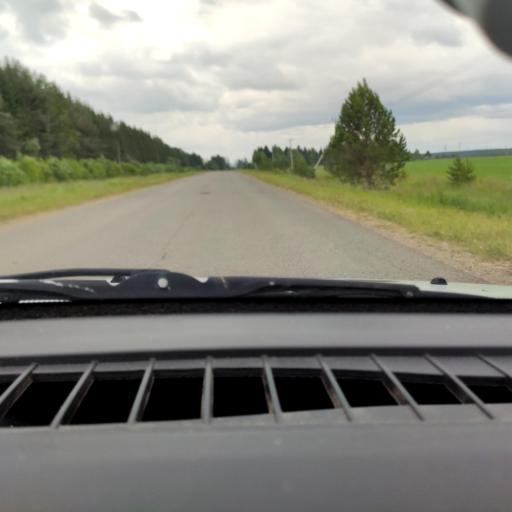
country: RU
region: Perm
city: Uinskoye
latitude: 57.1056
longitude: 56.6590
